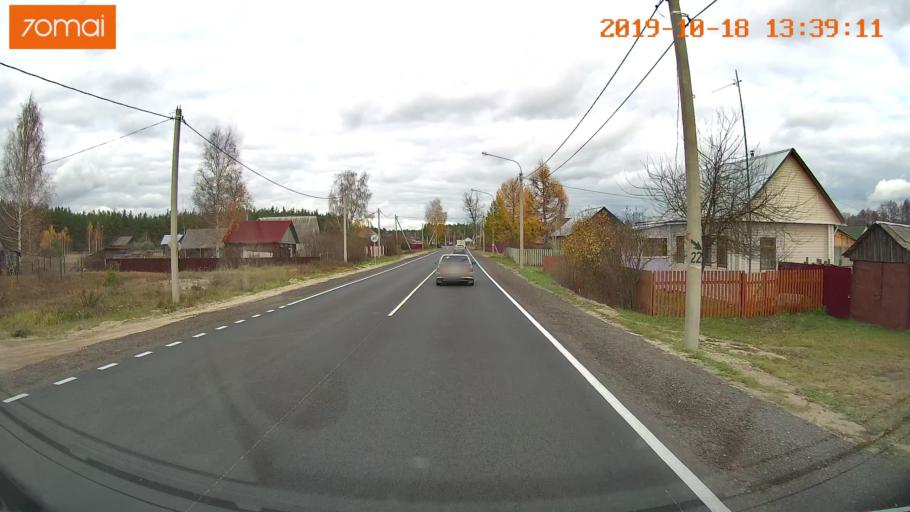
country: RU
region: Rjazan
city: Solotcha
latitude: 54.8964
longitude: 40.0005
